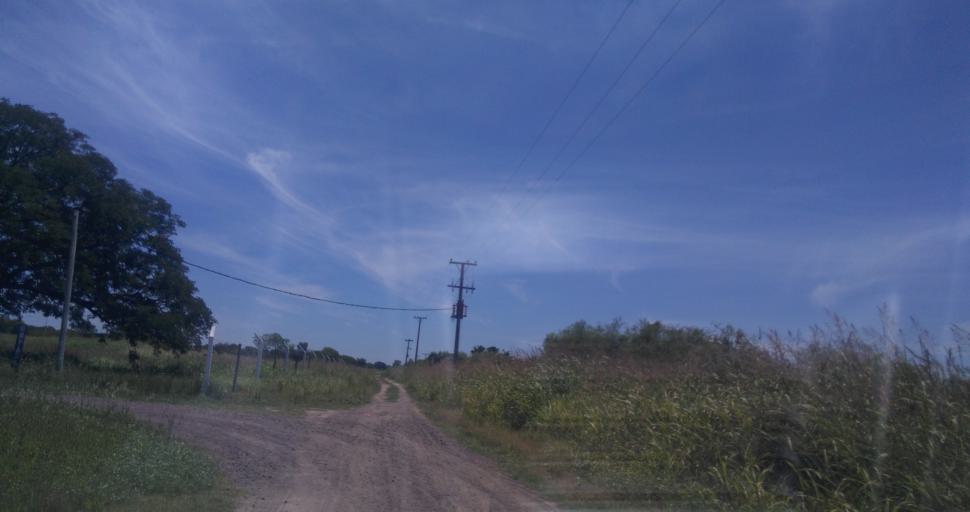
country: AR
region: Chaco
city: Fontana
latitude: -27.4342
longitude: -59.0351
